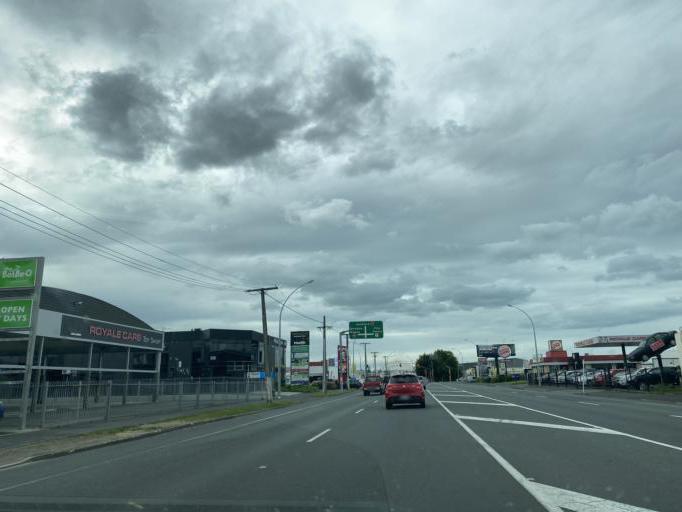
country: NZ
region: Waikato
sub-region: Hamilton City
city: Hamilton
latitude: -37.7910
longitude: 175.2600
